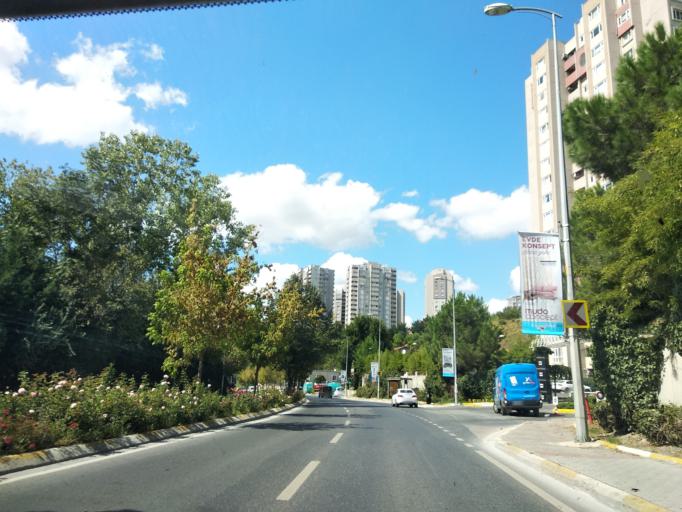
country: TR
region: Istanbul
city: Umraniye
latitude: 41.0054
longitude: 29.1124
